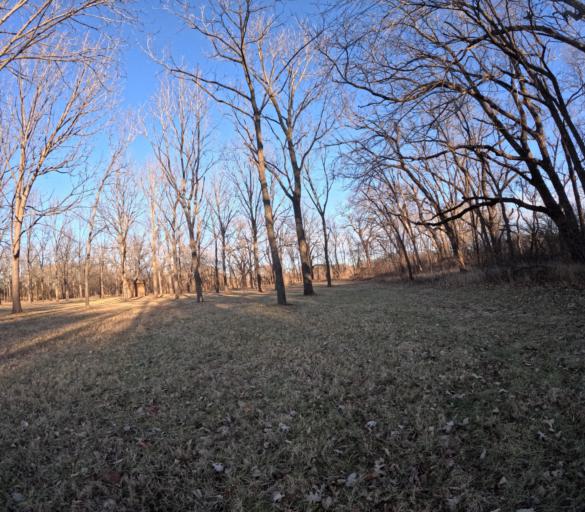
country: US
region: Kansas
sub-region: Riley County
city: Ogden
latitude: 39.2025
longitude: -96.6827
